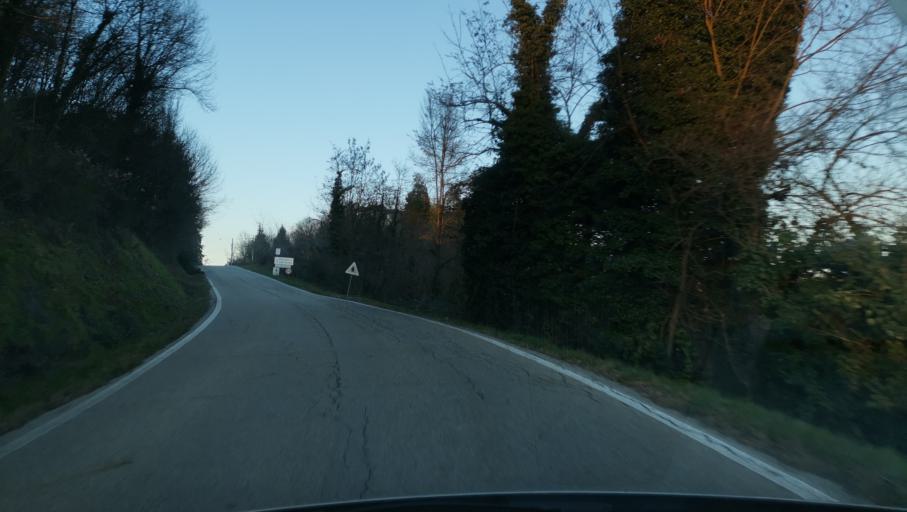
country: IT
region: Piedmont
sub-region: Provincia di Asti
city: Berzano di San Pietro
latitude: 45.0897
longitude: 7.9507
